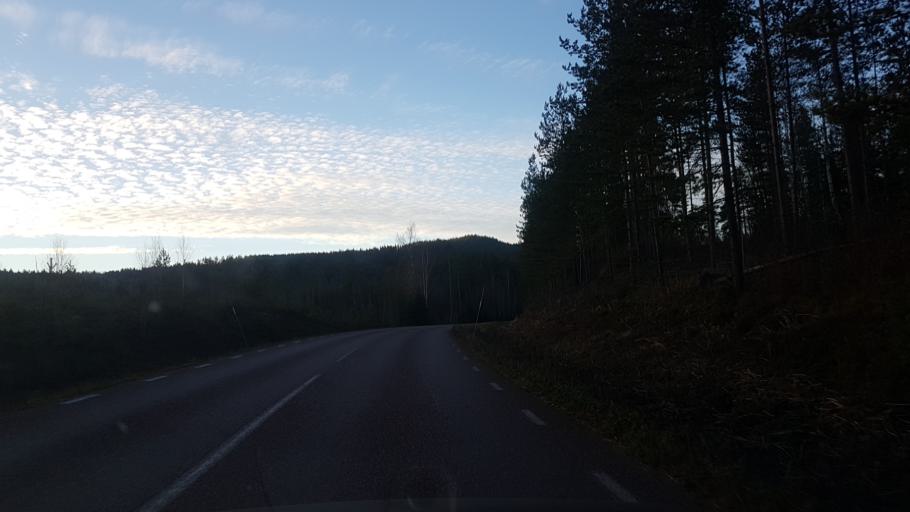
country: SE
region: Dalarna
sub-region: Faluns Kommun
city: Bjursas
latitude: 60.7244
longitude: 15.2568
